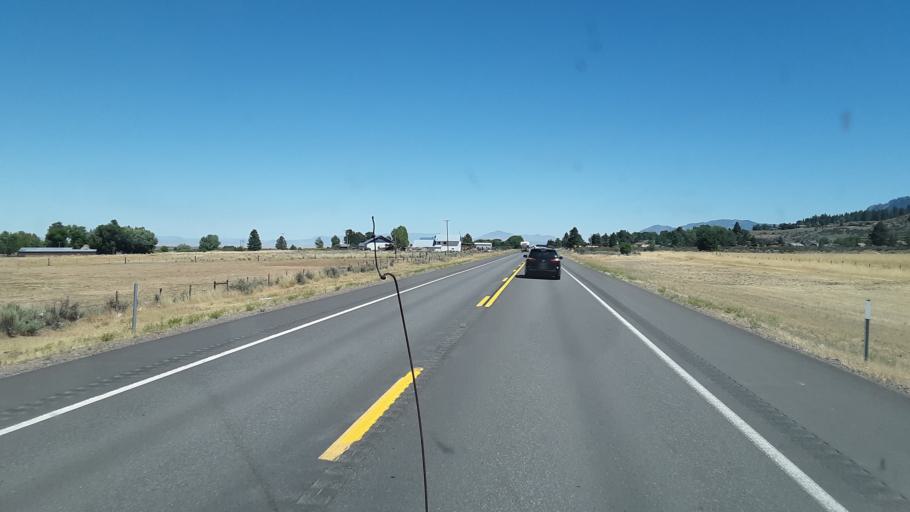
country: US
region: California
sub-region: Lassen County
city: Janesville
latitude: 40.2971
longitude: -120.5137
